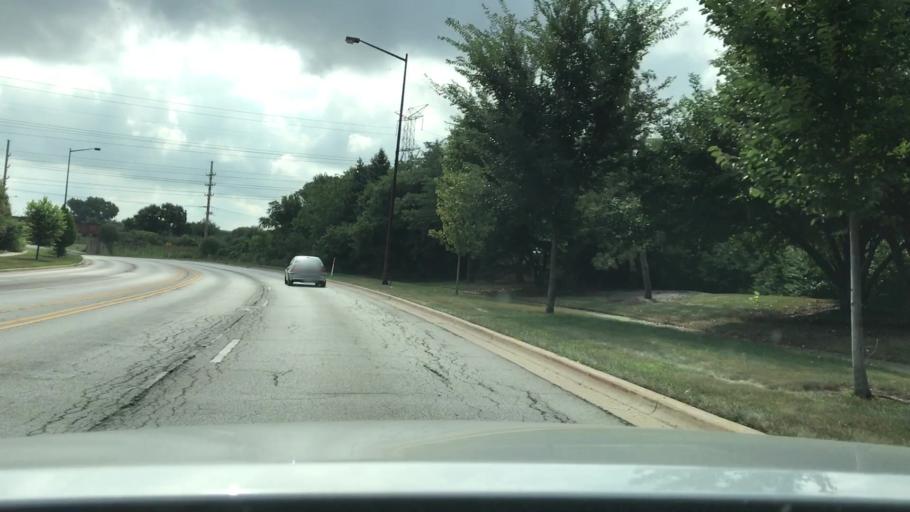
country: US
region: Illinois
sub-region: Kane County
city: Aurora
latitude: 41.7546
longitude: -88.2356
